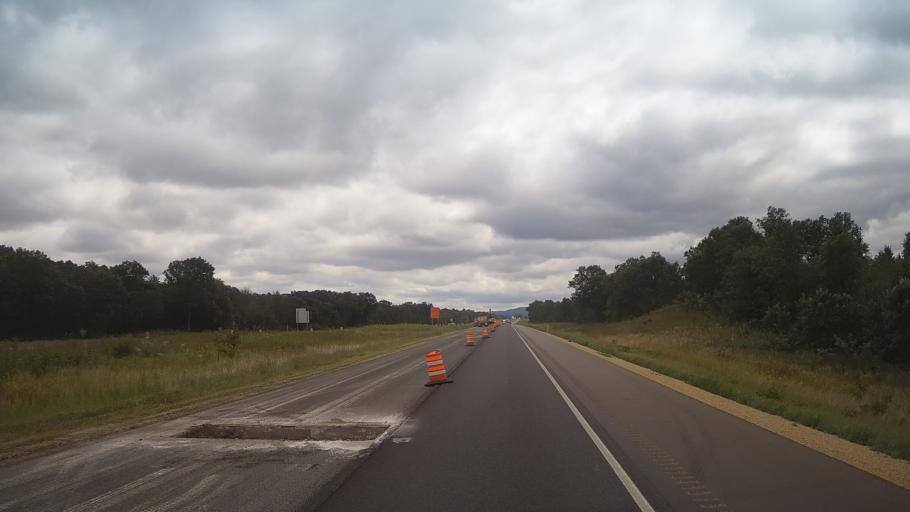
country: US
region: Wisconsin
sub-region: Monroe County
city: Sparta
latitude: 43.9434
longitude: -90.7440
